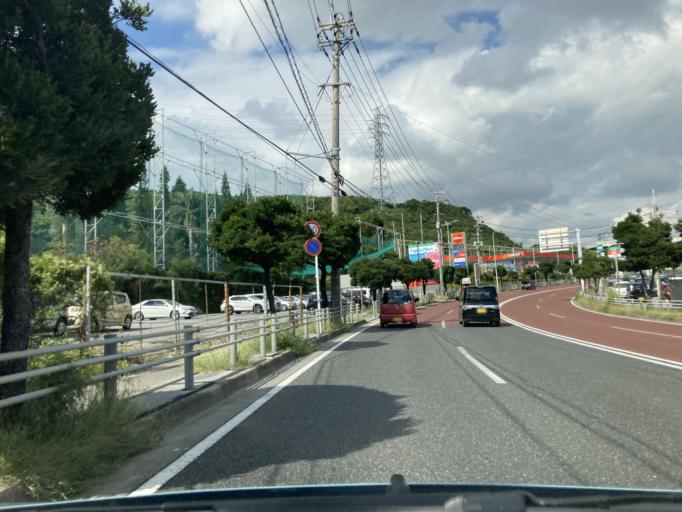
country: JP
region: Okinawa
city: Ginowan
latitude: 26.2354
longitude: 127.7696
